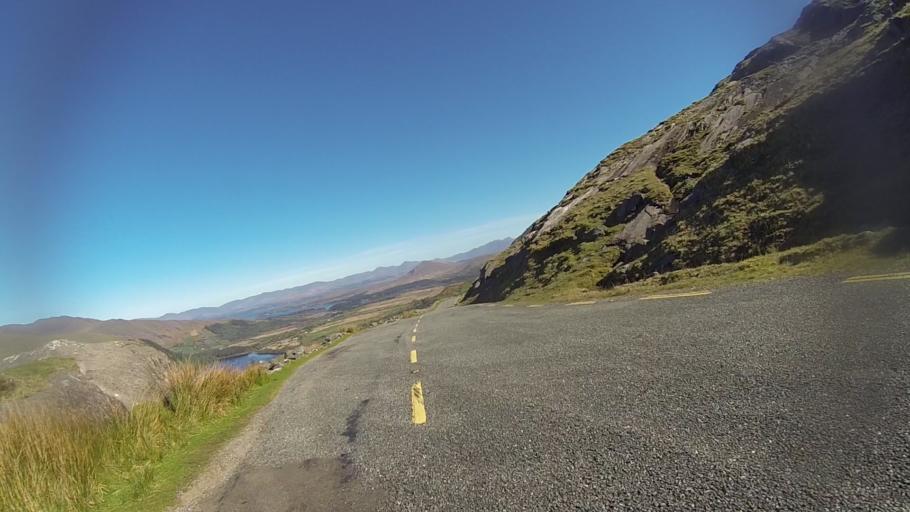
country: IE
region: Munster
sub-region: Ciarrai
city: Kenmare
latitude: 51.7245
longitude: -9.7581
